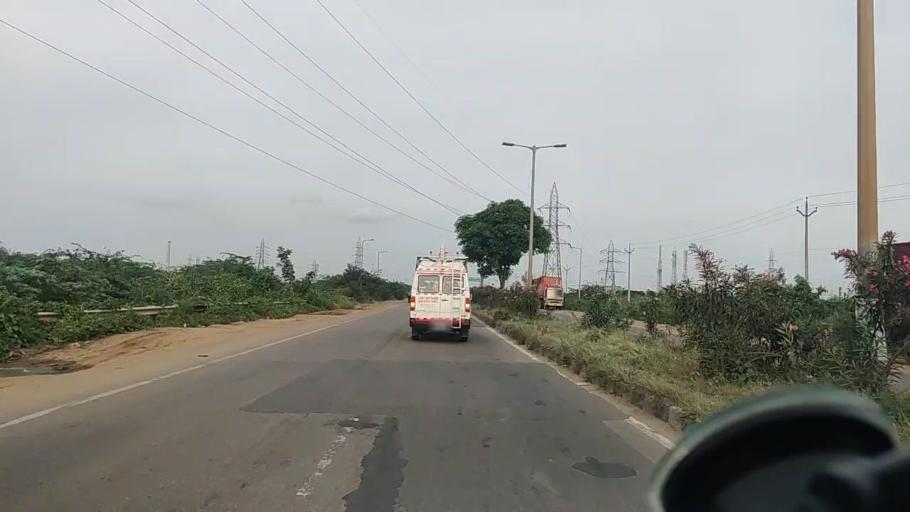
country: IN
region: Tamil Nadu
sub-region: Thiruvallur
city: Manali
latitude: 13.1817
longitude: 80.2661
